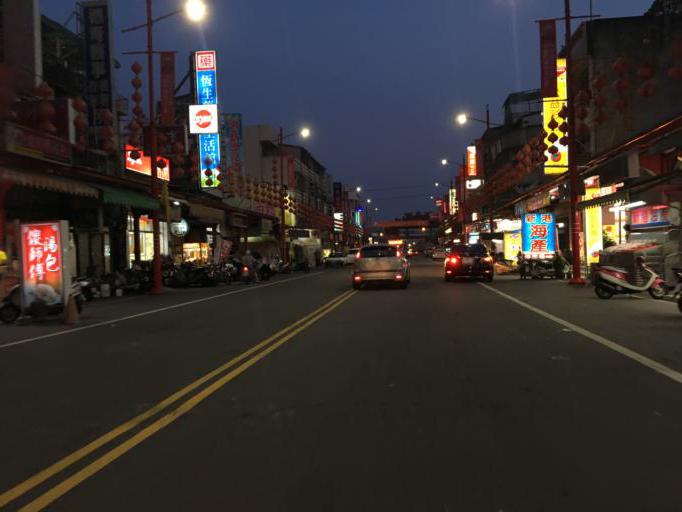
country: TW
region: Taiwan
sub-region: Chiayi
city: Taibao
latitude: 23.5537
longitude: 120.3474
